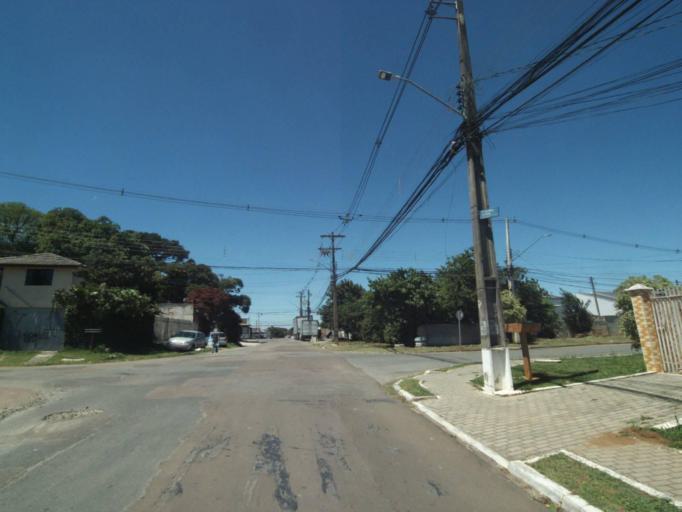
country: BR
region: Parana
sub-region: Curitiba
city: Curitiba
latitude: -25.4807
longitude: -49.3440
